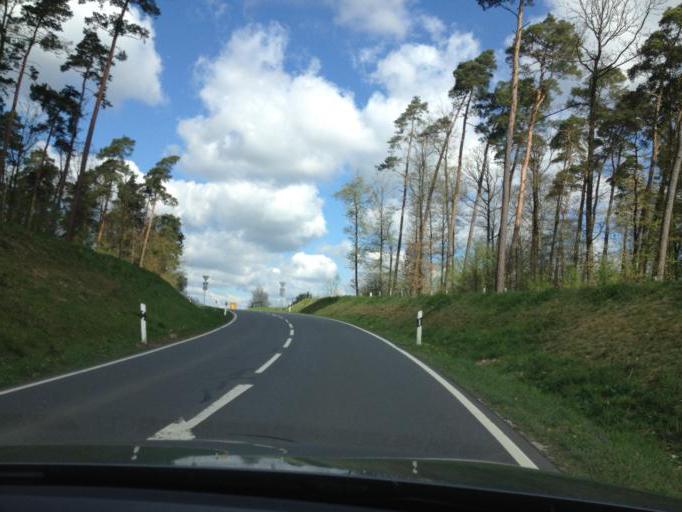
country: DE
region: Baden-Wuerttemberg
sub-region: Karlsruhe Region
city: Osterburken
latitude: 49.4167
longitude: 9.4488
